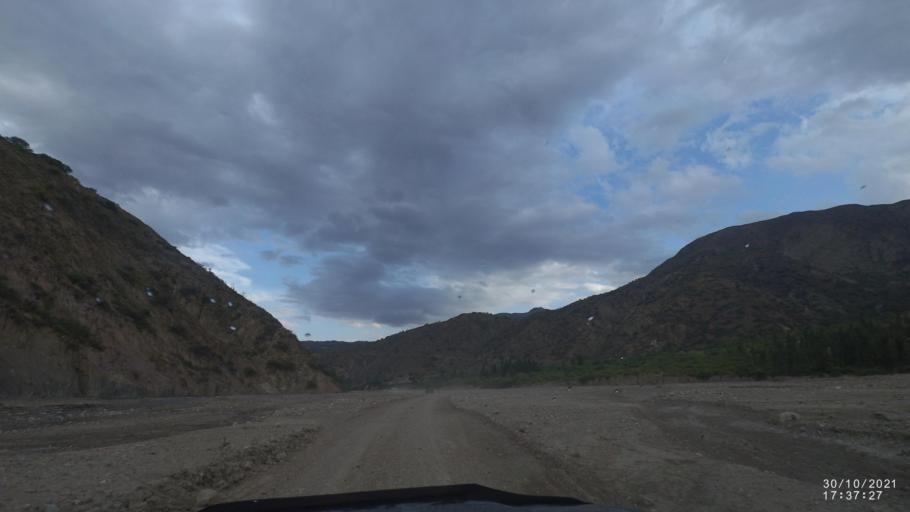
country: BO
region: Cochabamba
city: Sipe Sipe
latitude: -17.5265
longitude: -66.5610
